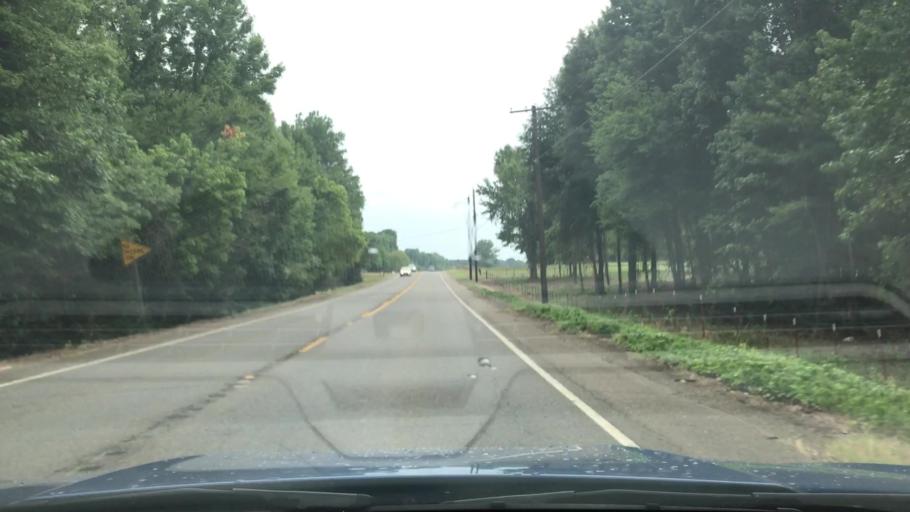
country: US
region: Texas
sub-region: Harrison County
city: Waskom
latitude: 32.4590
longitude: -94.0205
